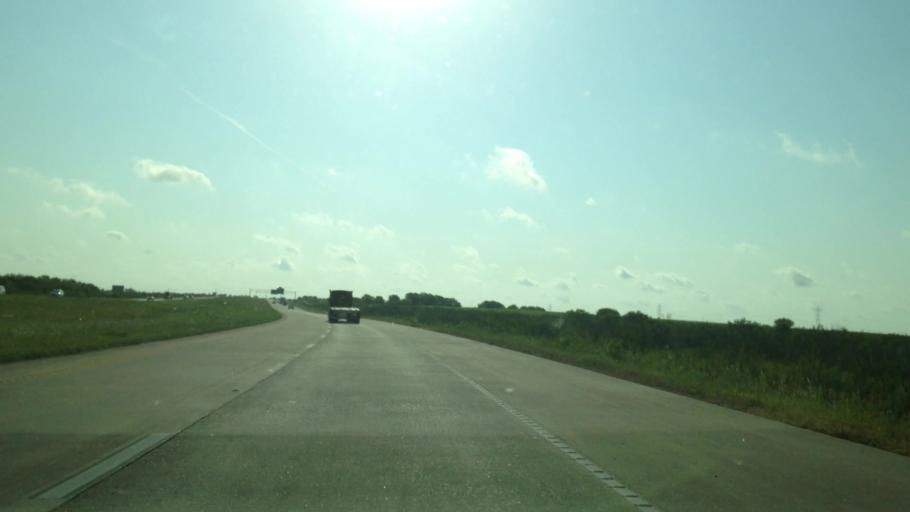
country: US
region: Texas
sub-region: Travis County
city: Onion Creek
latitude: 30.0807
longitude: -97.7259
